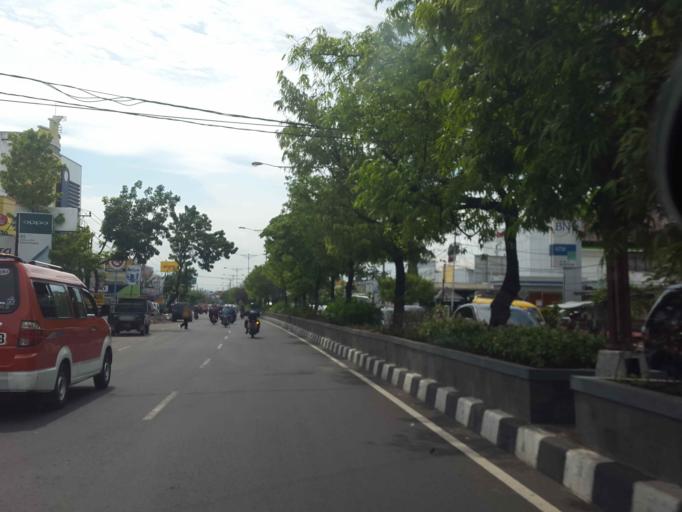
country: ID
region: Central Java
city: Semarang
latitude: -6.9818
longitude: 110.3944
